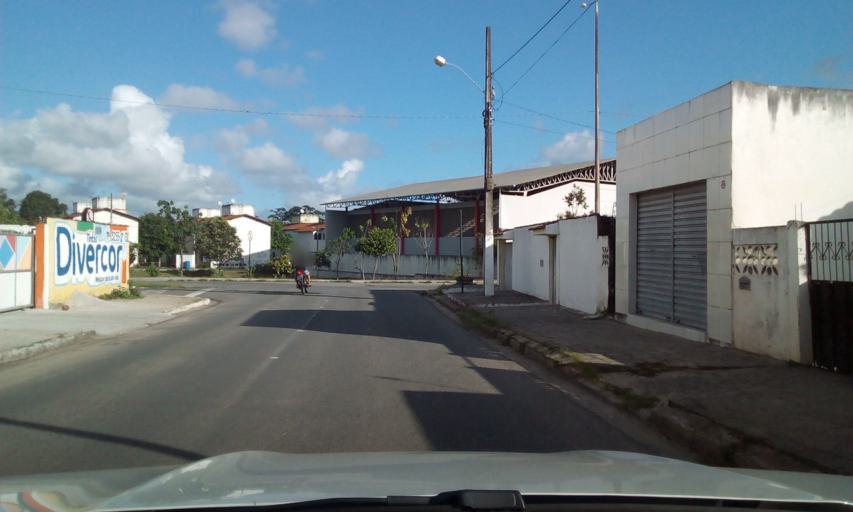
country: BR
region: Paraiba
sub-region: Bayeux
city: Bayeux
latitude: -7.1780
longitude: -34.9146
